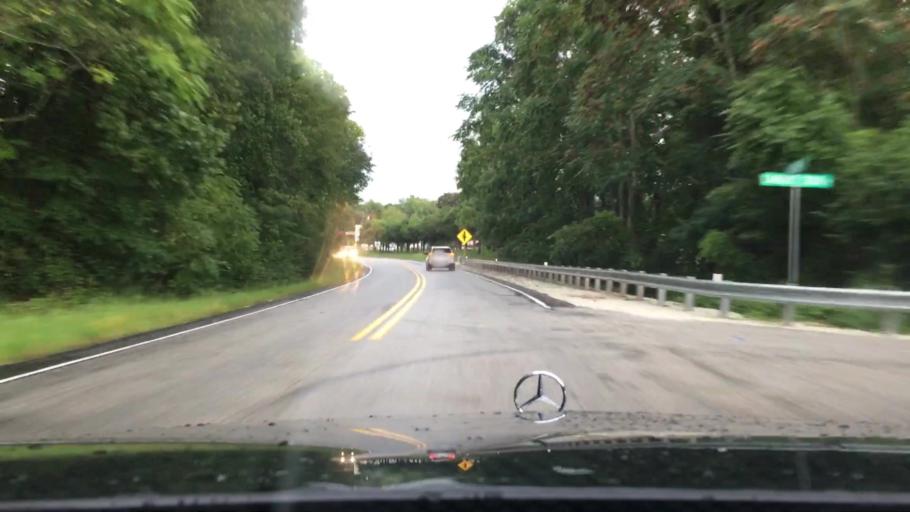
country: US
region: Virginia
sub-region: Amherst County
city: Amherst
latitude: 37.6814
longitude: -79.0225
